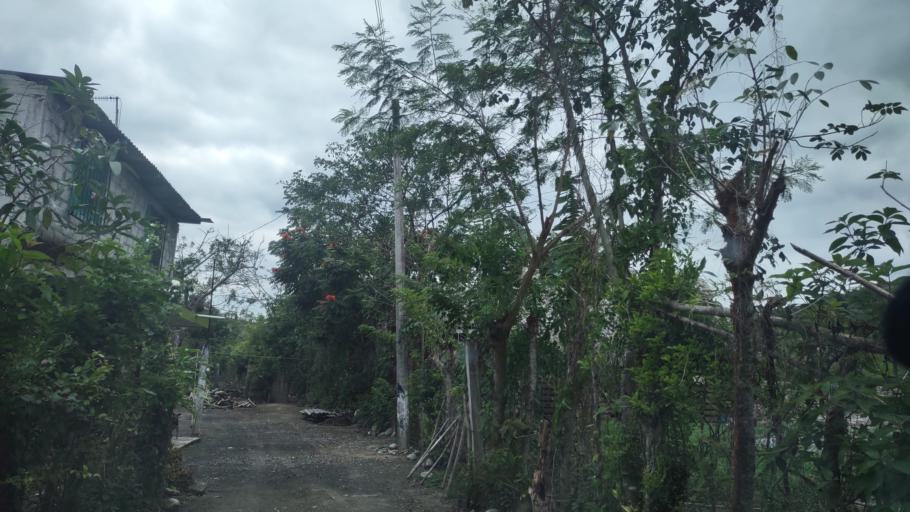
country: MX
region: Veracruz
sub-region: Papantla
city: Polutla
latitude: 20.4683
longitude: -97.2574
